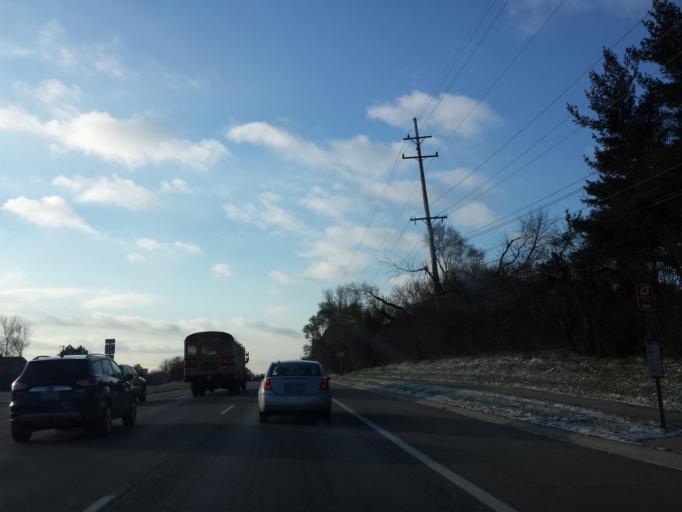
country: US
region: Michigan
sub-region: Oakland County
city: Bingham Farms
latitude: 42.5291
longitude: -83.2855
